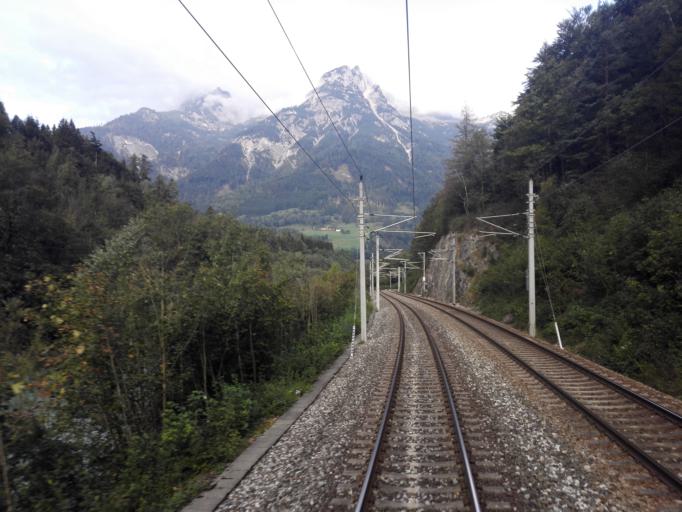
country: AT
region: Salzburg
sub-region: Politischer Bezirk Sankt Johann im Pongau
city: Werfen
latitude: 47.4893
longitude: 13.1825
